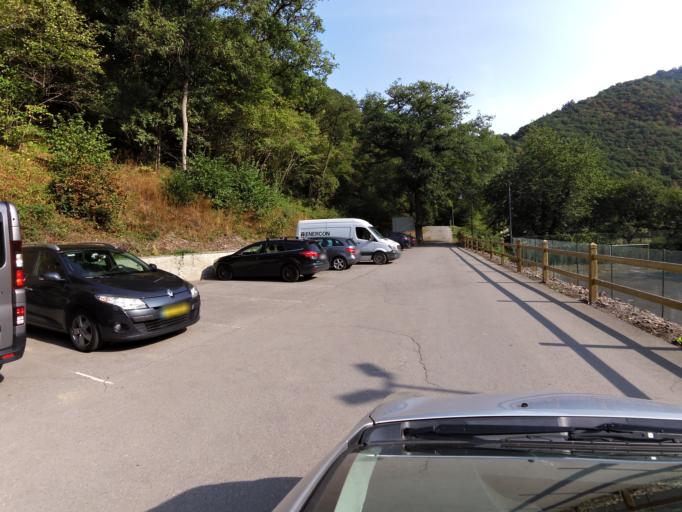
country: LU
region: Diekirch
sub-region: Canton de Diekirch
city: Bourscheid
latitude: 49.9123
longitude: 6.0831
